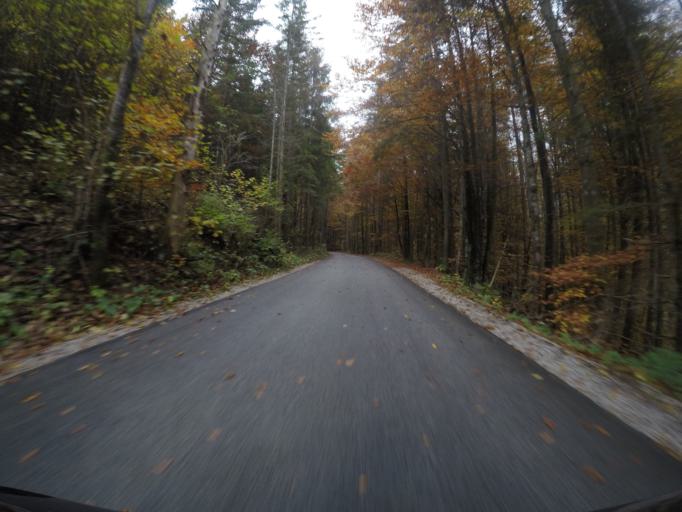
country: SI
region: Jesenice
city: Hrusica
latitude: 46.4069
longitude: 13.9988
